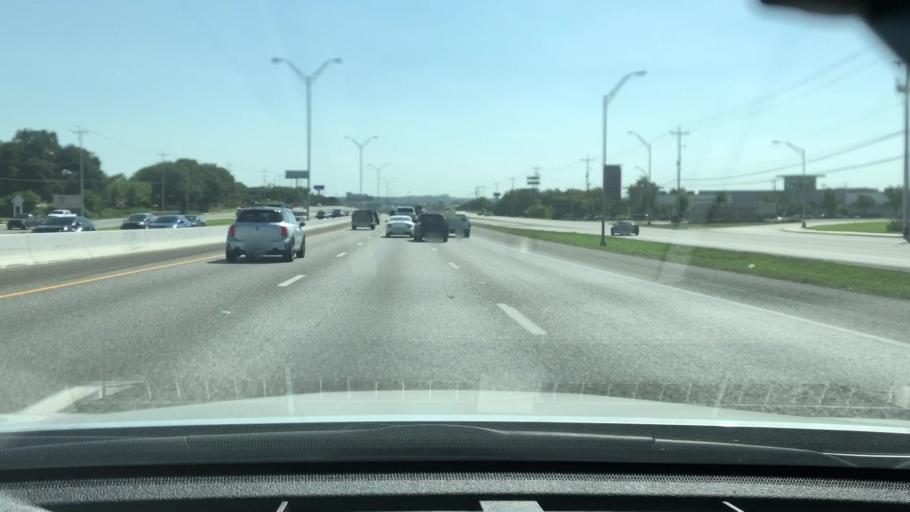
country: US
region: Texas
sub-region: Bexar County
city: Selma
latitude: 29.5966
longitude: -98.2841
